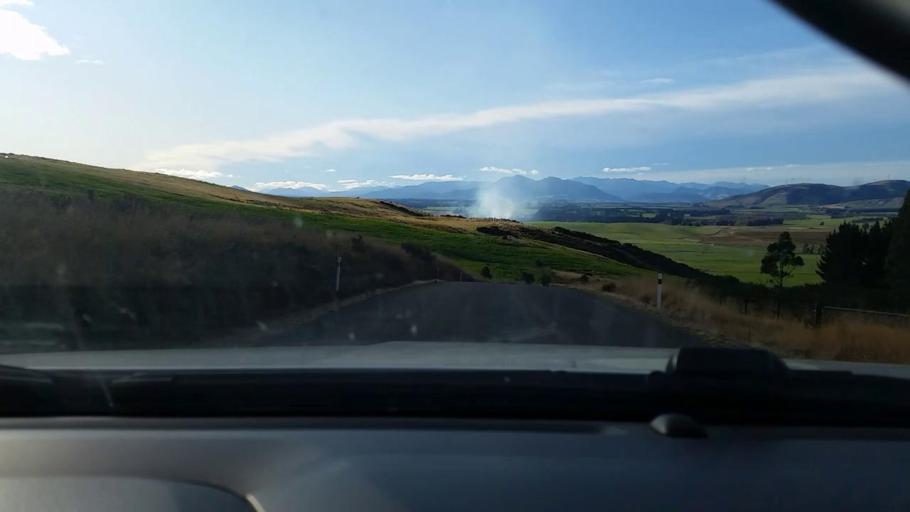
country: NZ
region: Southland
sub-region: Southland District
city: Winton
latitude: -45.8203
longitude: 168.1738
